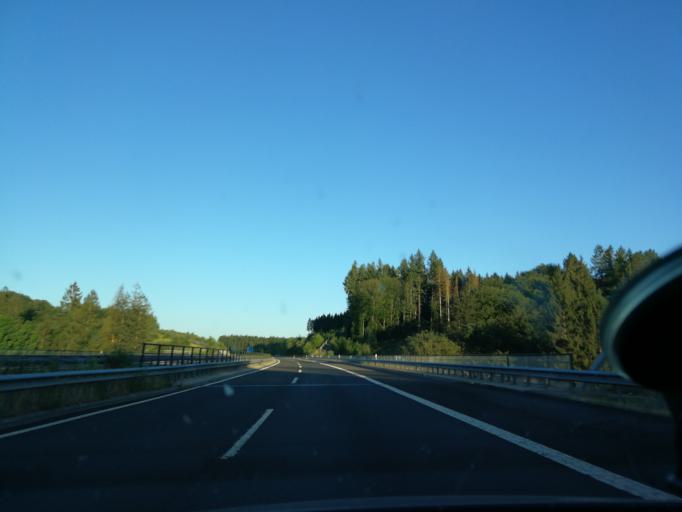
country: DE
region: Rheinland-Pfalz
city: Horscheid
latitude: 50.2136
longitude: 6.8678
